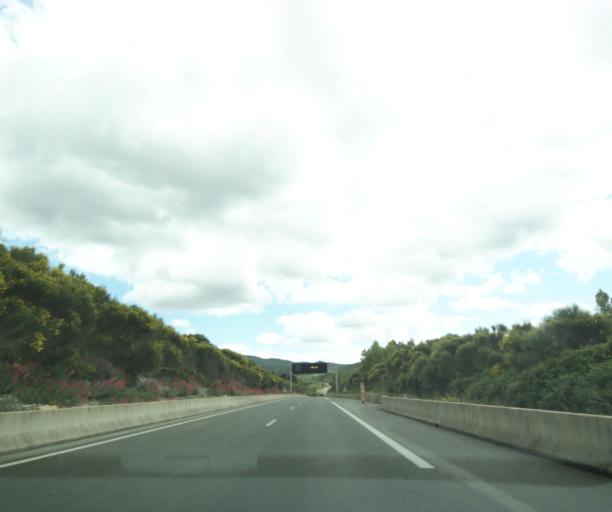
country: FR
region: Languedoc-Roussillon
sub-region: Departement de l'Herault
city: Lodeve
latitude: 43.7737
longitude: 3.3326
